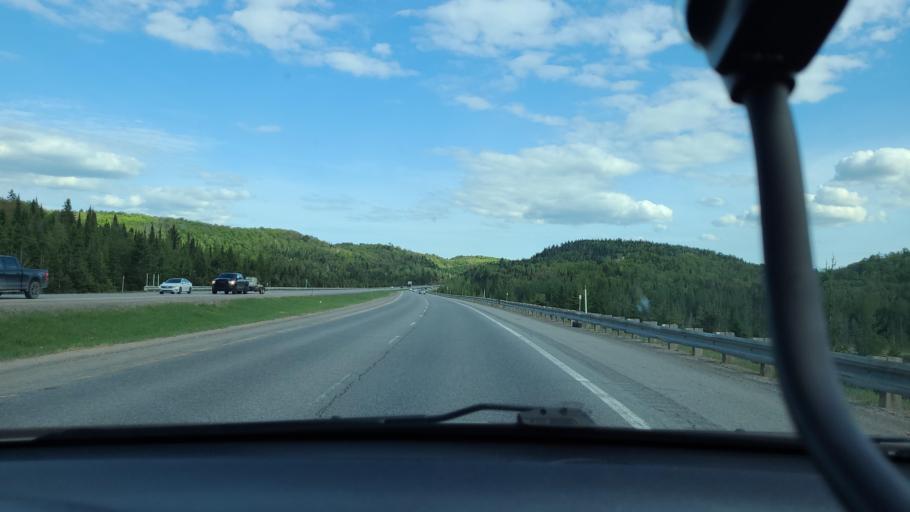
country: CA
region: Quebec
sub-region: Laurentides
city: Val-David
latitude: 46.0002
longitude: -74.2263
